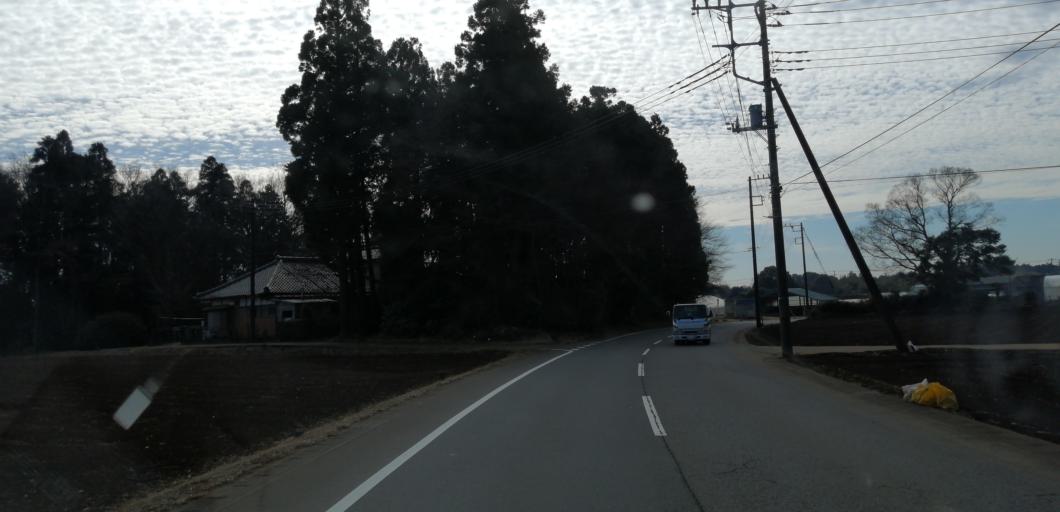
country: JP
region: Chiba
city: Narita
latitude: 35.7667
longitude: 140.3632
